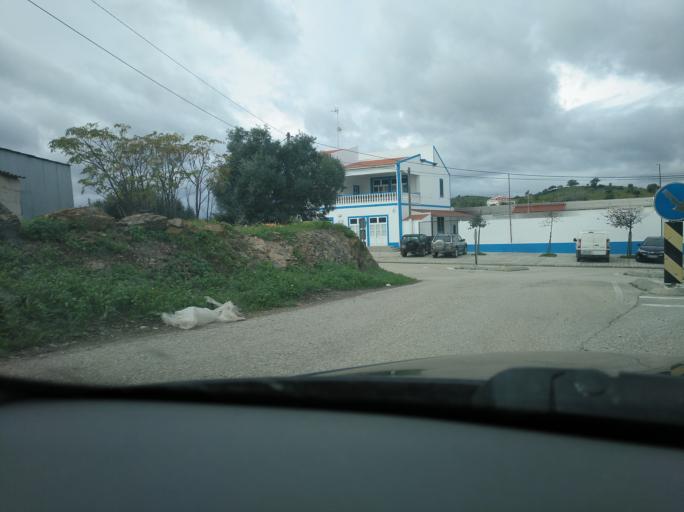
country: PT
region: Faro
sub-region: Castro Marim
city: Castro Marim
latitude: 37.2204
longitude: -7.4890
